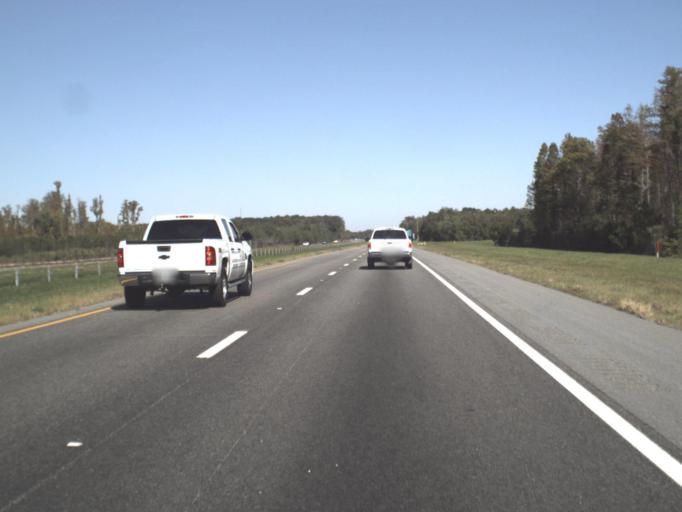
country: US
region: Florida
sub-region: Pasco County
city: Shady Hills
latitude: 28.2995
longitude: -82.5502
